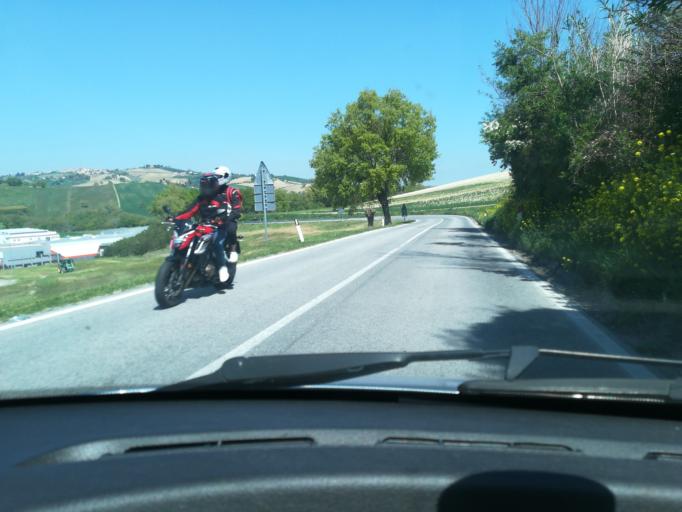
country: IT
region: The Marches
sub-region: Provincia di Macerata
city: Strada
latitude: 43.4027
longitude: 13.2051
